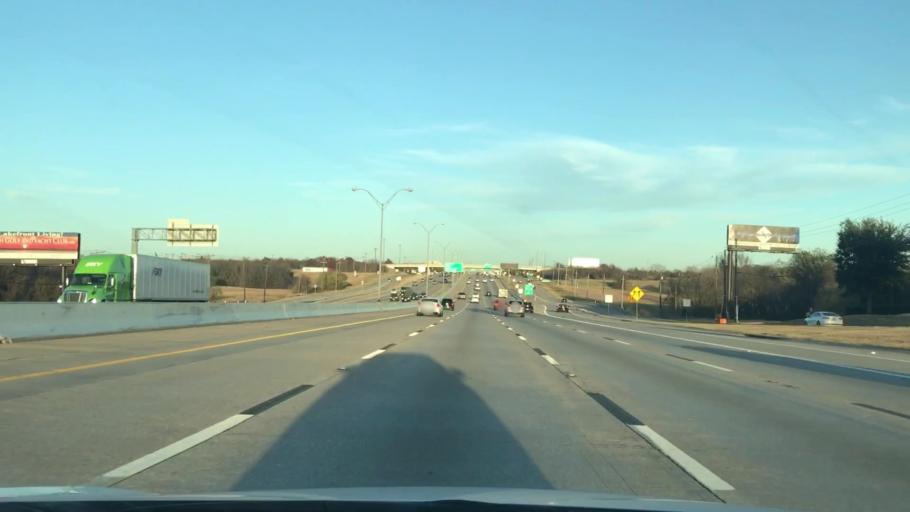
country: US
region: Texas
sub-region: Dallas County
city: Sunnyvale
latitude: 32.8429
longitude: -96.5894
